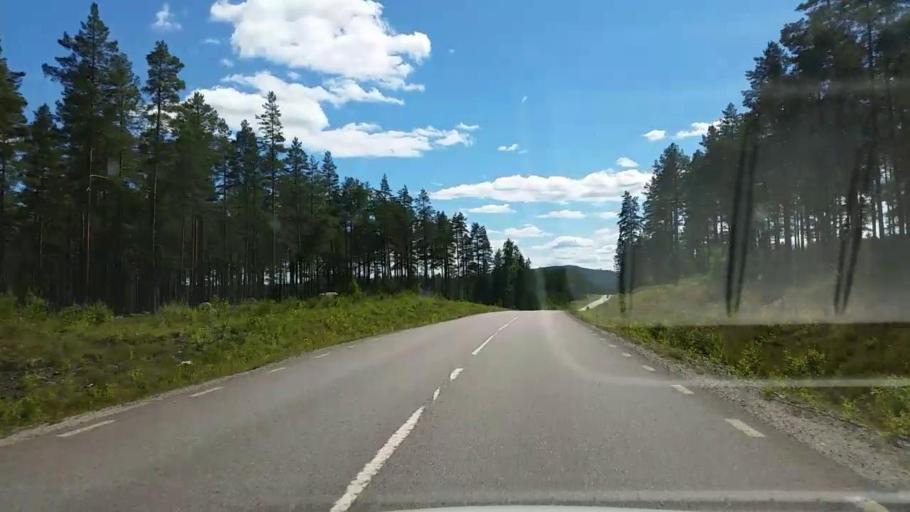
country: SE
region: Dalarna
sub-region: Faluns Kommun
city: Svardsjo
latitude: 61.0238
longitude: 15.7592
